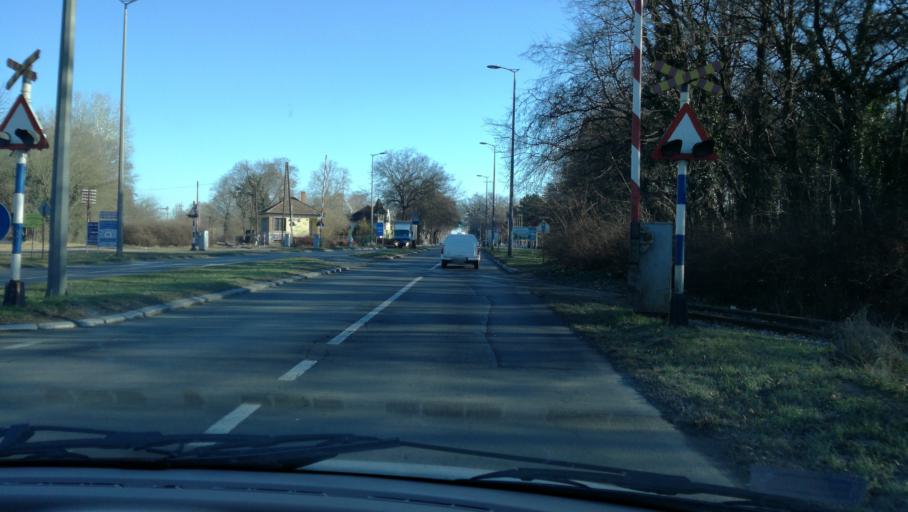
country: RS
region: Autonomna Pokrajina Vojvodina
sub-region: Severnobacki Okrug
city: Subotica
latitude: 46.1026
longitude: 19.7561
